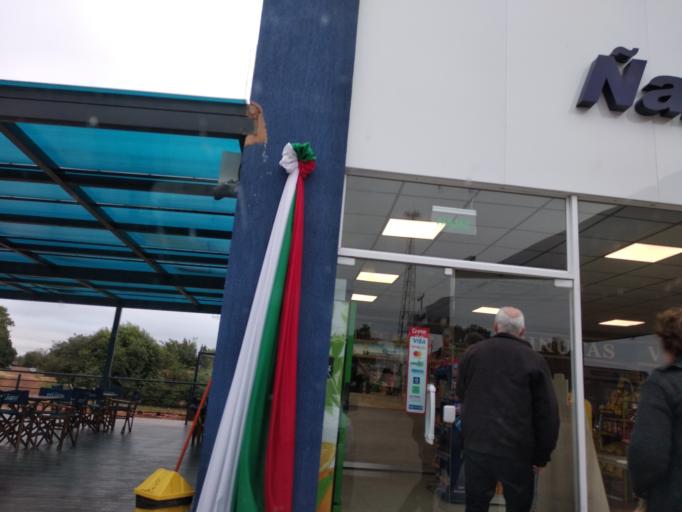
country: PY
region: Misiones
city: Santa Maria
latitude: -26.8810
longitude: -57.0108
